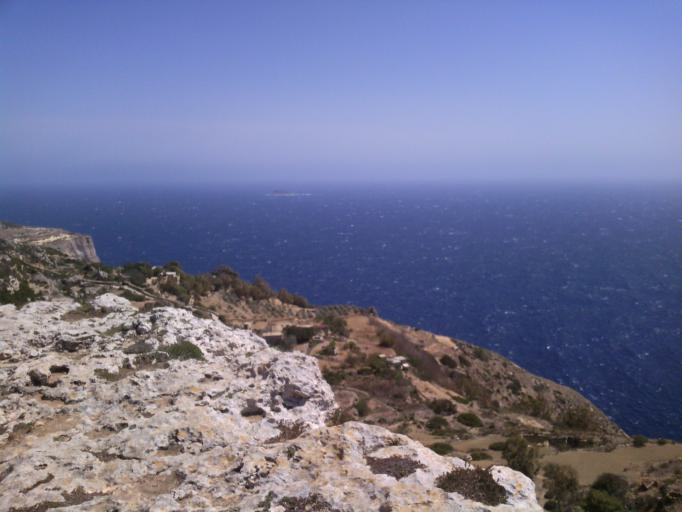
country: MT
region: Dingli
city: Dingli
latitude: 35.8515
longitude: 14.3860
